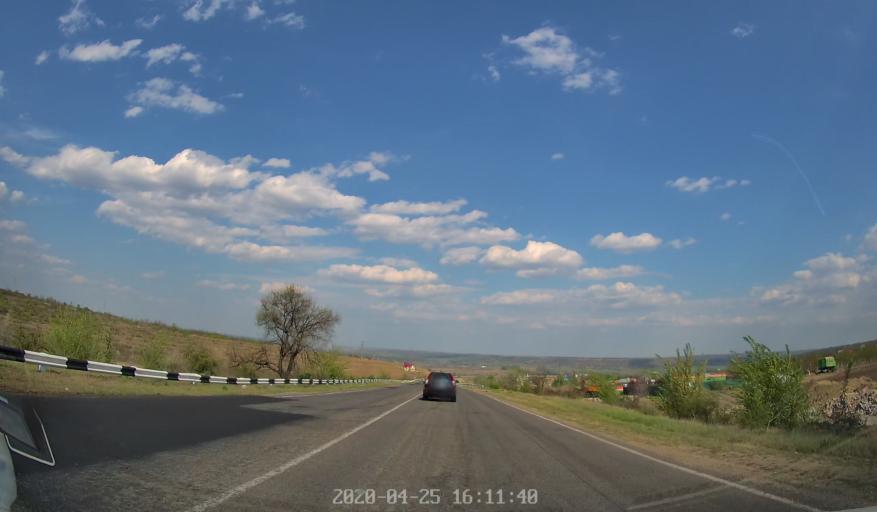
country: MD
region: Chisinau
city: Vadul lui Voda
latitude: 47.0889
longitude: 29.0597
